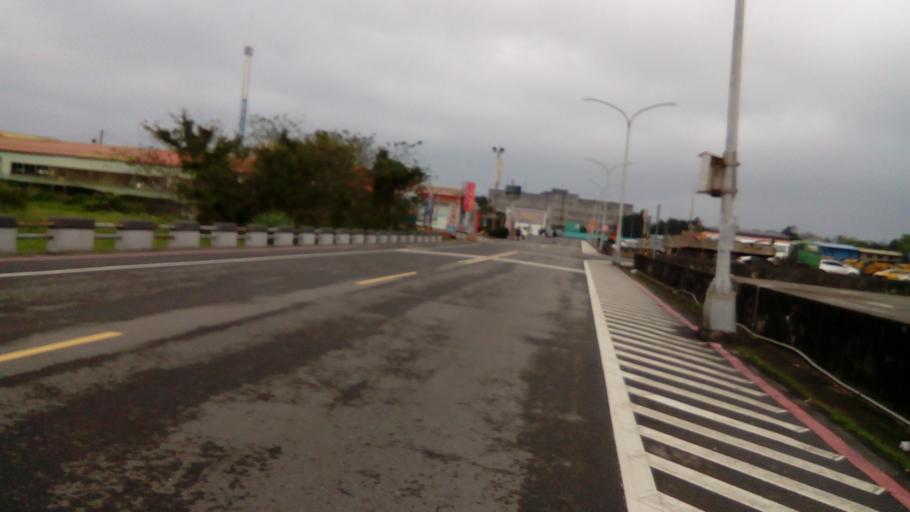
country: TW
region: Taipei
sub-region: Taipei
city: Banqiao
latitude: 25.1798
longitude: 121.4202
